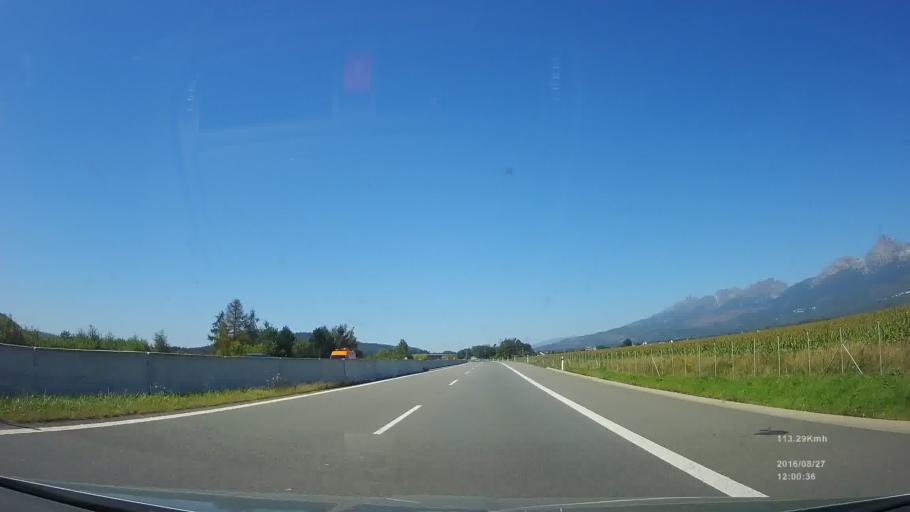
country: SK
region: Presovsky
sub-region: Okres Poprad
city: Svit
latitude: 49.0638
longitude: 20.2020
